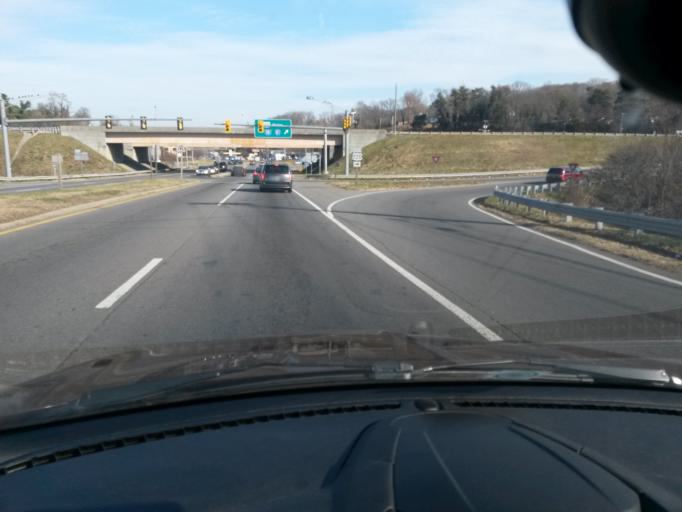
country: US
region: Virginia
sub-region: Roanoke County
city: Narrows
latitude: 37.2312
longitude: -79.9741
